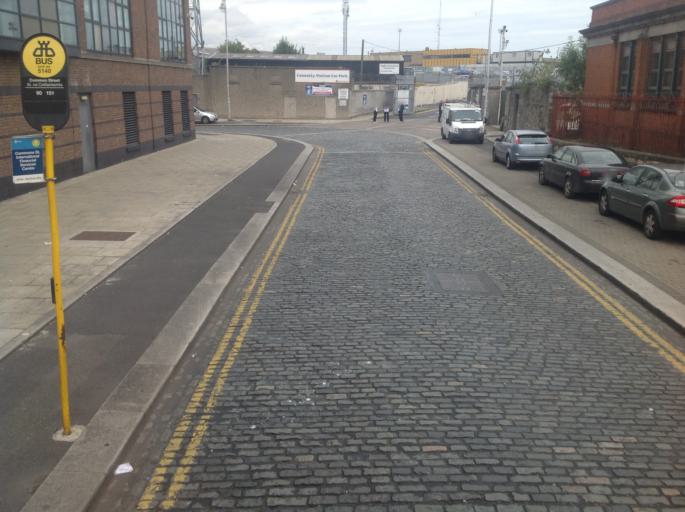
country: IE
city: Fairview
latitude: 53.3511
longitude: -6.2455
